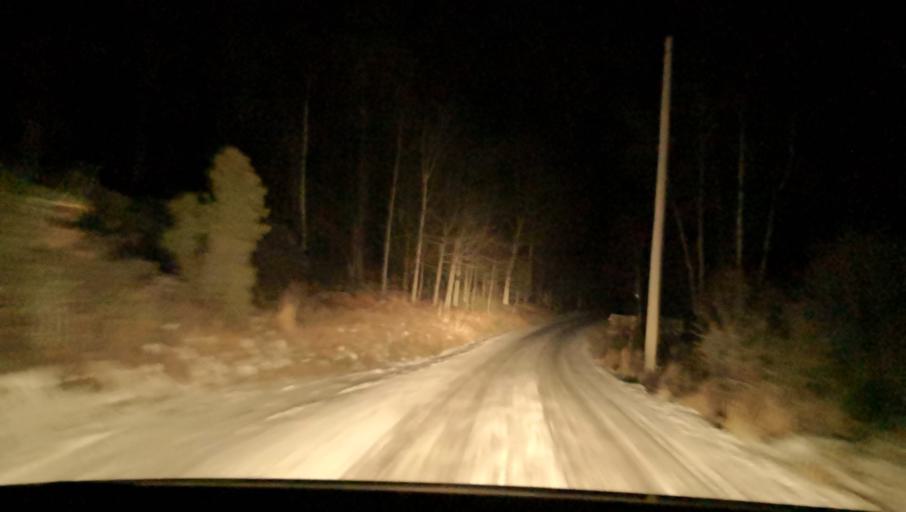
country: SE
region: Stockholm
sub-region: Tyreso Kommun
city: Bollmora
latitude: 59.2777
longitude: 18.2306
